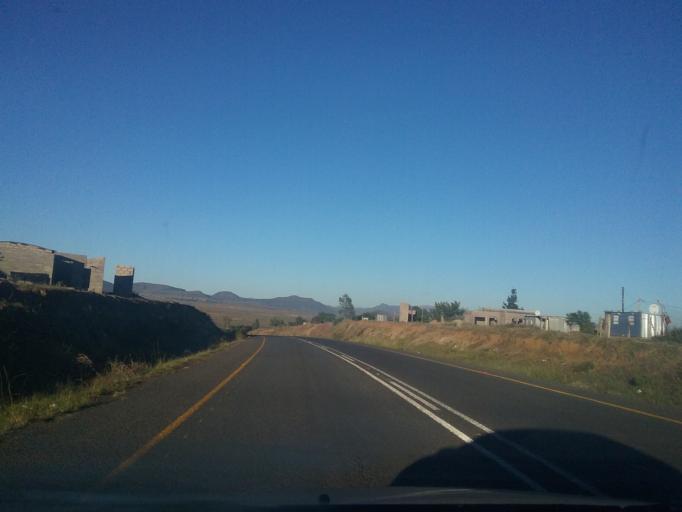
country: LS
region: Mohale's Hoek District
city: Mohale's Hoek
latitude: -30.1514
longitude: 27.4428
